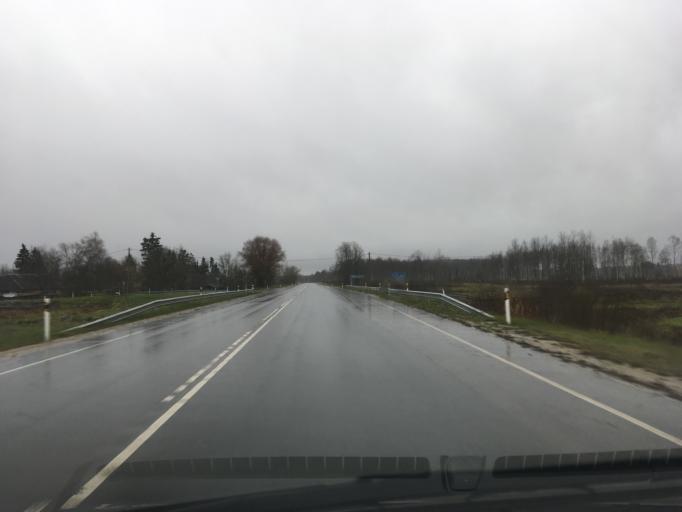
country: EE
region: Harju
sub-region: Nissi vald
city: Turba
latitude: 58.8614
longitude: 24.0746
